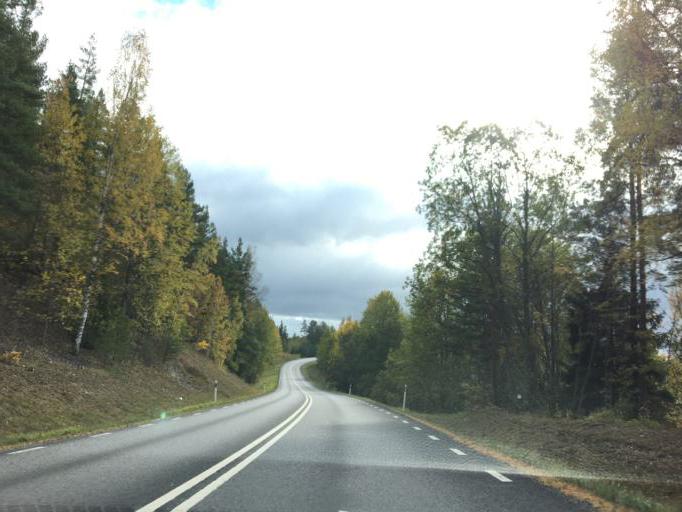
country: SE
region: Soedermanland
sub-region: Katrineholms Kommun
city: Katrineholm
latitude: 58.9322
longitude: 16.4077
